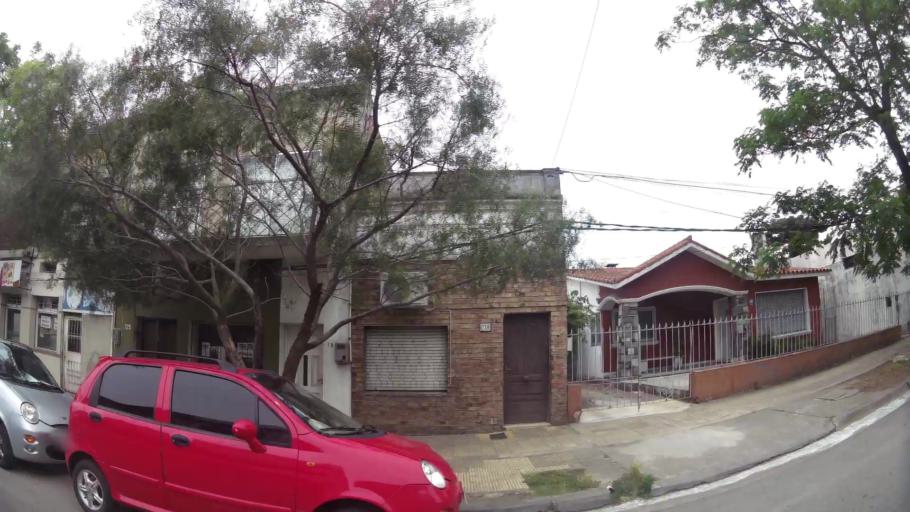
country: UY
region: Canelones
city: Las Piedras
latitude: -34.7281
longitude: -56.2207
